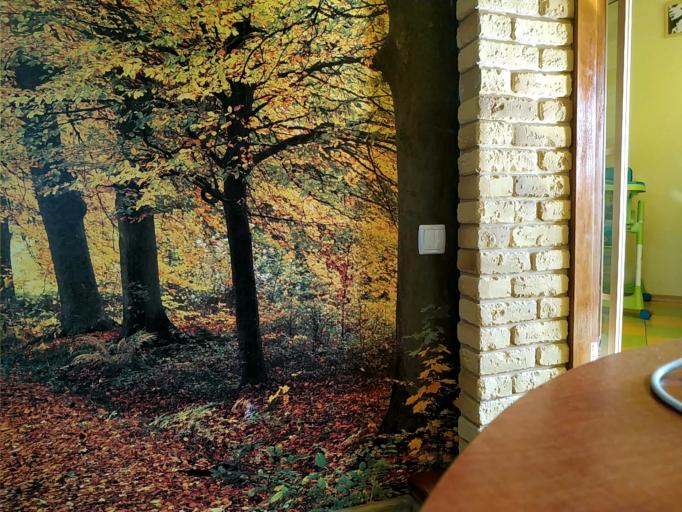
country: RU
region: Tverskaya
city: Kalashnikovo
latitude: 57.3422
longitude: 35.2584
